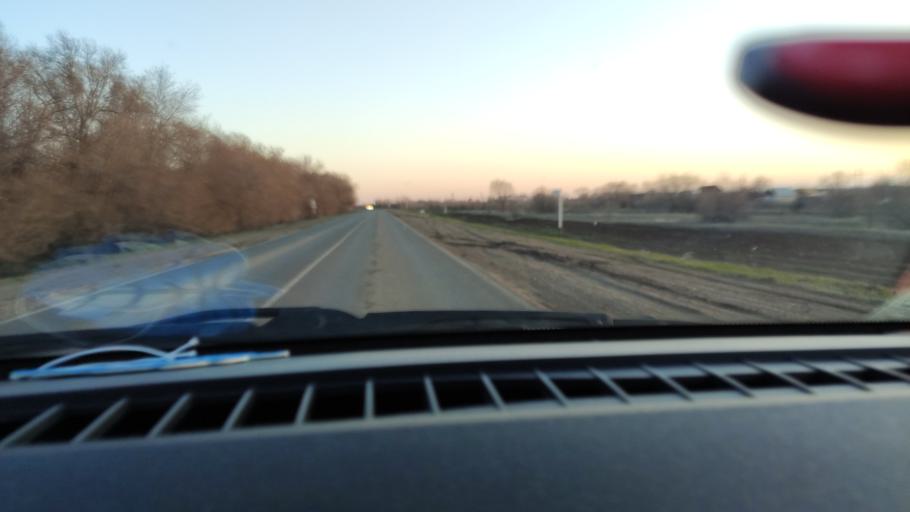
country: RU
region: Saratov
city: Privolzhskiy
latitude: 51.3406
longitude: 46.0410
